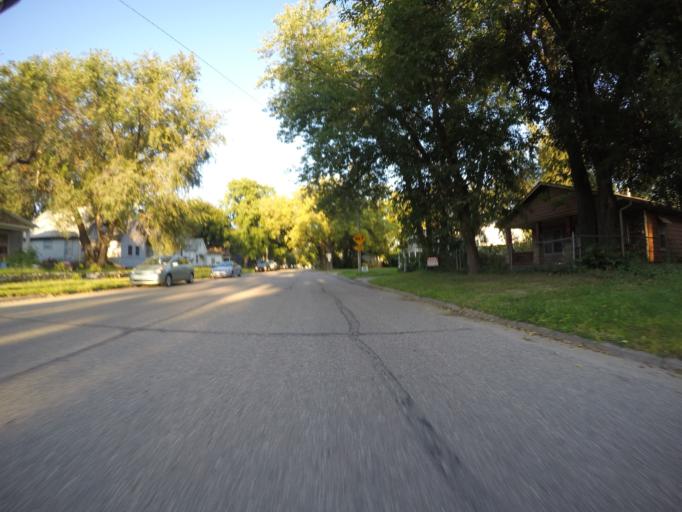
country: US
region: Kansas
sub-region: Riley County
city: Manhattan
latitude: 39.1753
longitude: -96.5748
